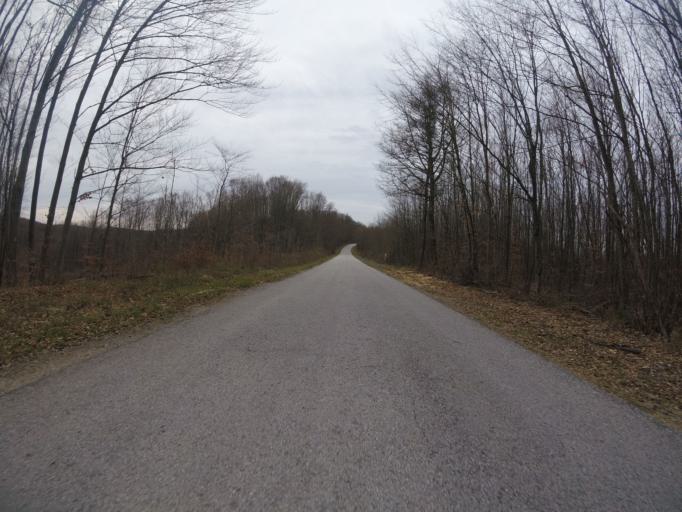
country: HR
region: Grad Zagreb
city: Strmec
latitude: 45.6189
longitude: 15.9240
